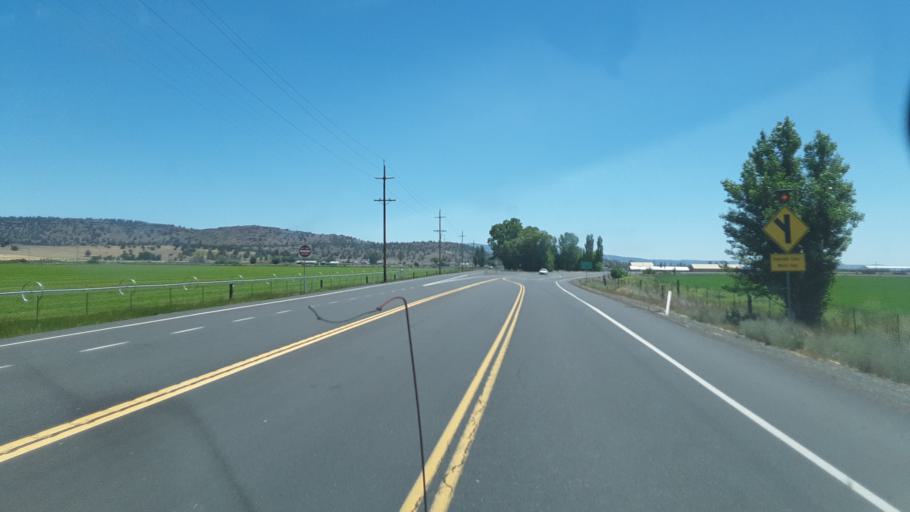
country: US
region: California
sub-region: Siskiyou County
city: Tulelake
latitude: 42.0240
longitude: -121.5526
